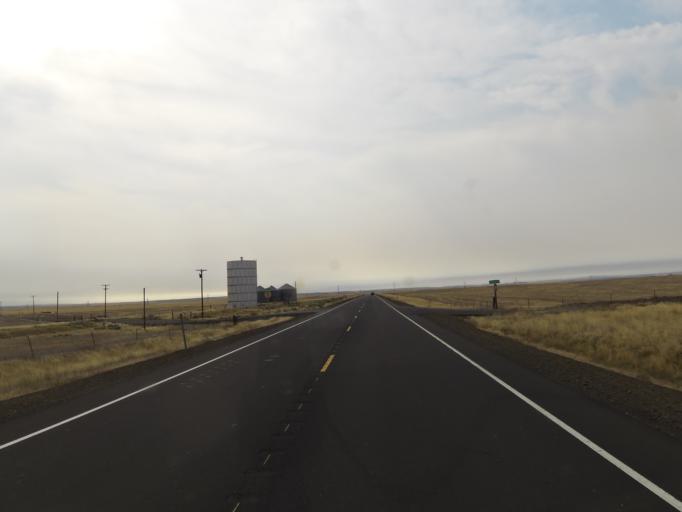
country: US
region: Oregon
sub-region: Sherman County
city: Moro
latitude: 45.3019
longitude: -120.7635
